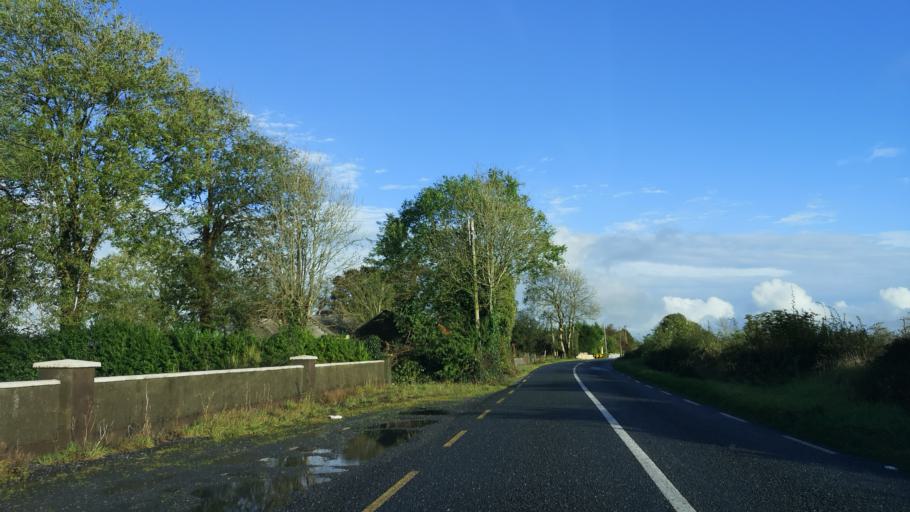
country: IE
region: Connaught
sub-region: Roscommon
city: Castlerea
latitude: 53.8083
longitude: -8.5151
